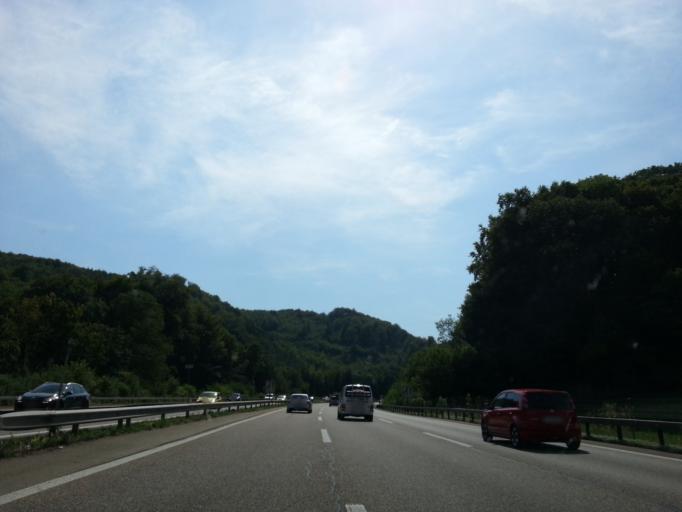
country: CH
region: Basel-Landschaft
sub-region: Bezirk Liestal
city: Arisdorf
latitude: 47.4965
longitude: 7.7670
